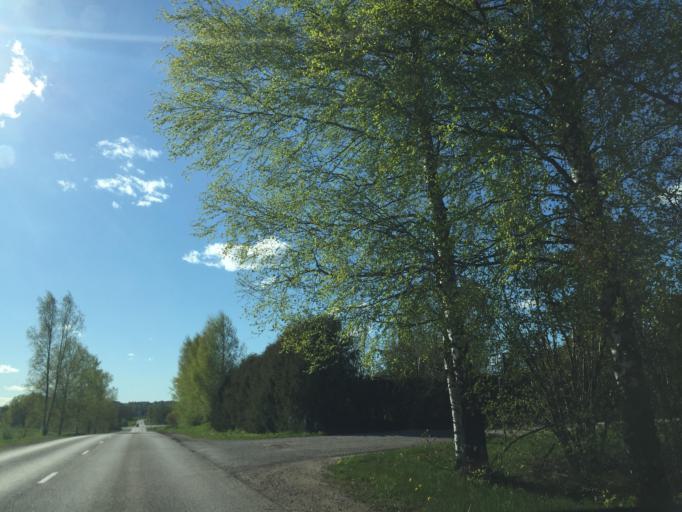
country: LV
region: Madonas Rajons
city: Madona
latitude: 56.8058
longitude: 26.0378
